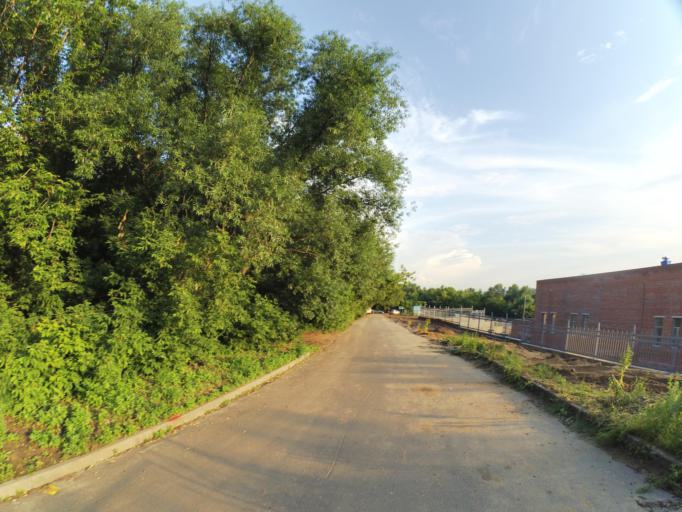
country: RU
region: Moscow
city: Shchukino
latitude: 55.8045
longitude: 37.4496
